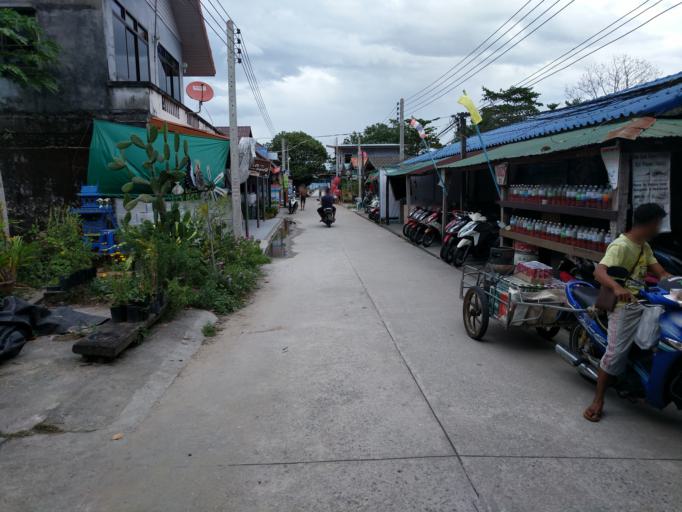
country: TH
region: Ranong
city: Kapoe
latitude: 9.7403
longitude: 98.4209
